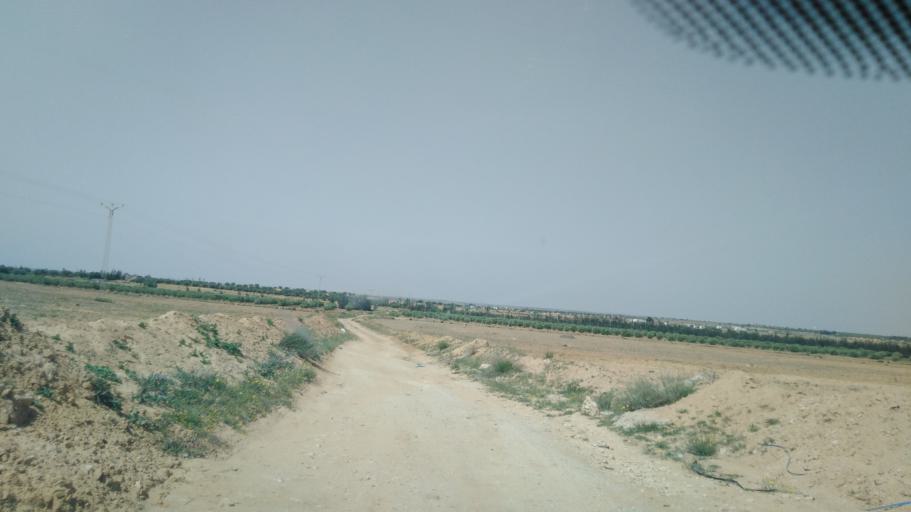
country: TN
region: Safaqis
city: Sfax
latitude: 34.7520
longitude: 10.5610
